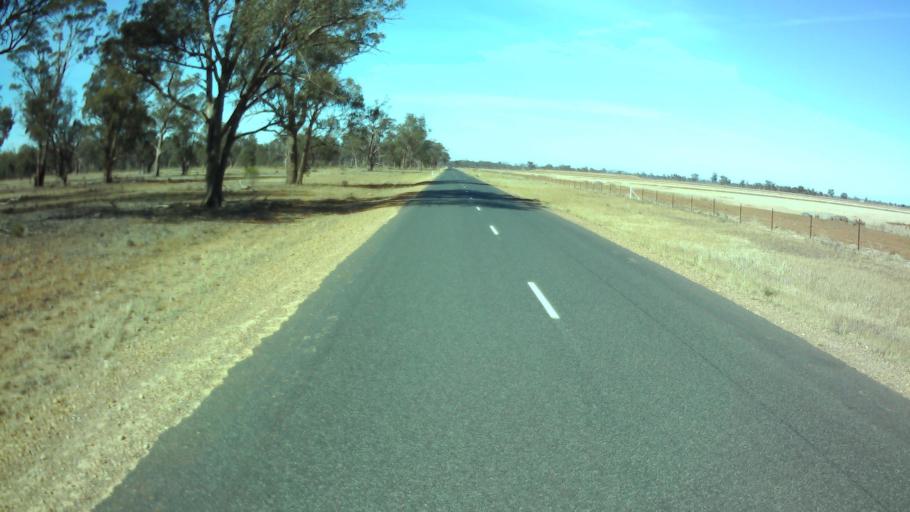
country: AU
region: New South Wales
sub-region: Weddin
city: Grenfell
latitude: -34.1206
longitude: 147.8118
